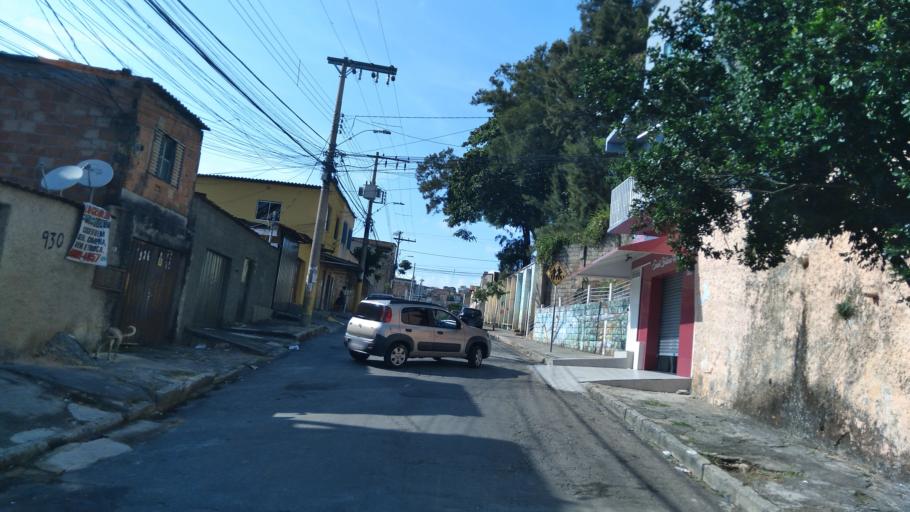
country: BR
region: Minas Gerais
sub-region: Belo Horizonte
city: Belo Horizonte
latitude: -19.8974
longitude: -43.9405
